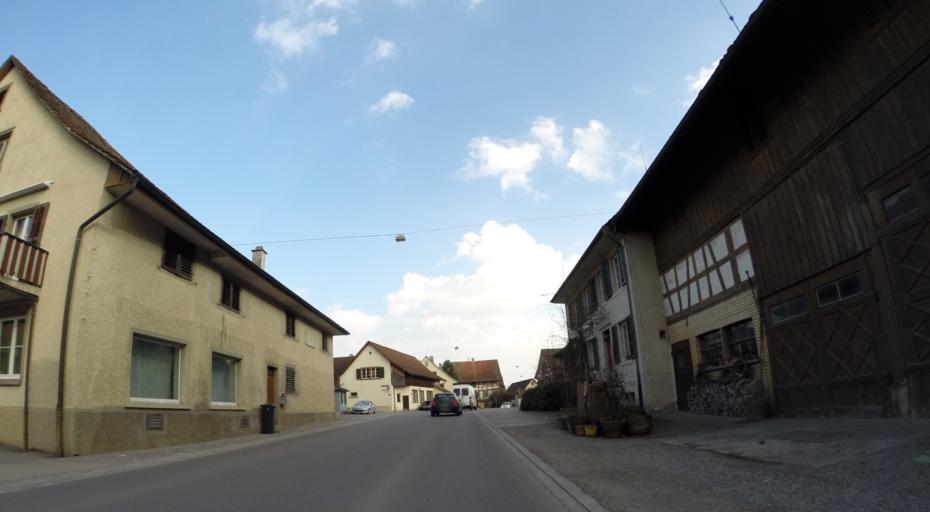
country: CH
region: Thurgau
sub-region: Frauenfeld District
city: Wagenhausen
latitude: 47.6332
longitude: 8.7977
